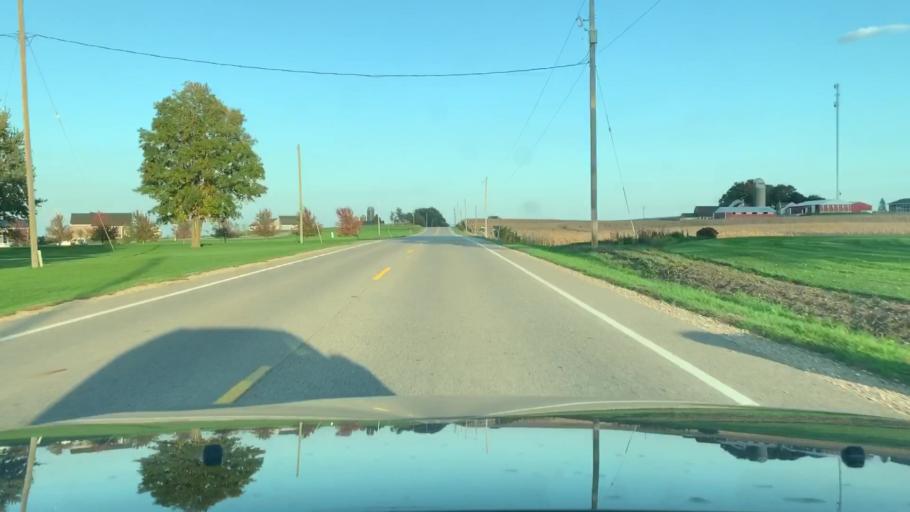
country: US
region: Michigan
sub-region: Ottawa County
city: Hudsonville
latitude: 42.8114
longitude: -85.8282
